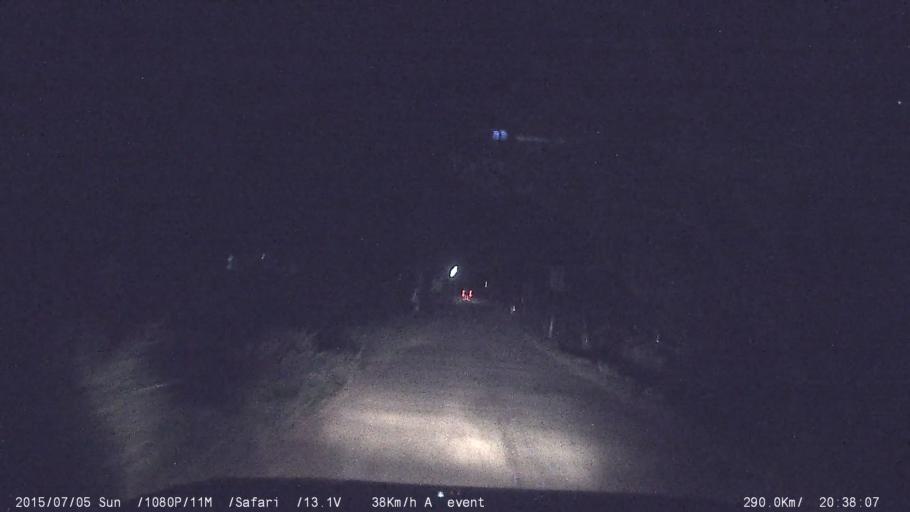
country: IN
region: Kerala
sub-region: Palakkad district
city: Mannarakkat
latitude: 10.9843
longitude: 76.4948
